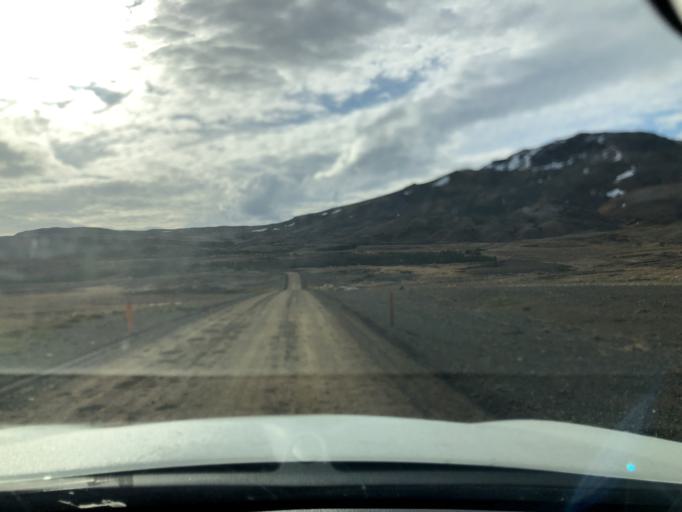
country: IS
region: West
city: Stykkisholmur
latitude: 64.9966
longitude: -22.7498
